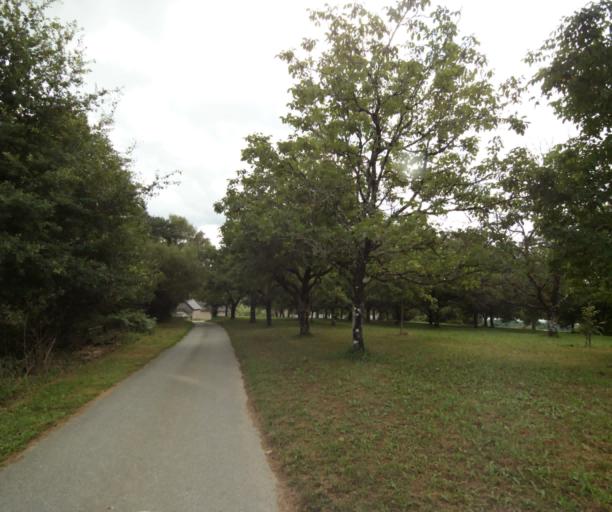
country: FR
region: Limousin
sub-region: Departement de la Correze
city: Sainte-Fortunade
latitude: 45.1709
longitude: 1.8385
